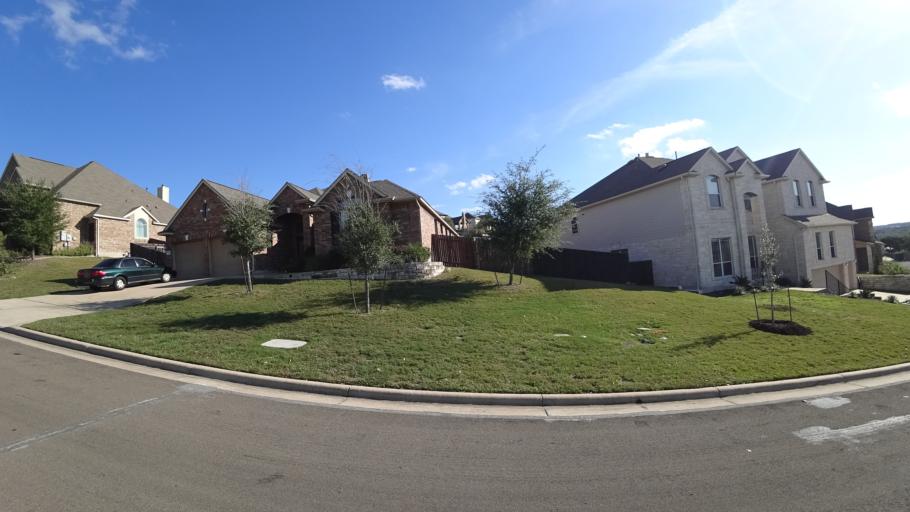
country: US
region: Texas
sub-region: Travis County
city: Barton Creek
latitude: 30.2497
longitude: -97.8789
